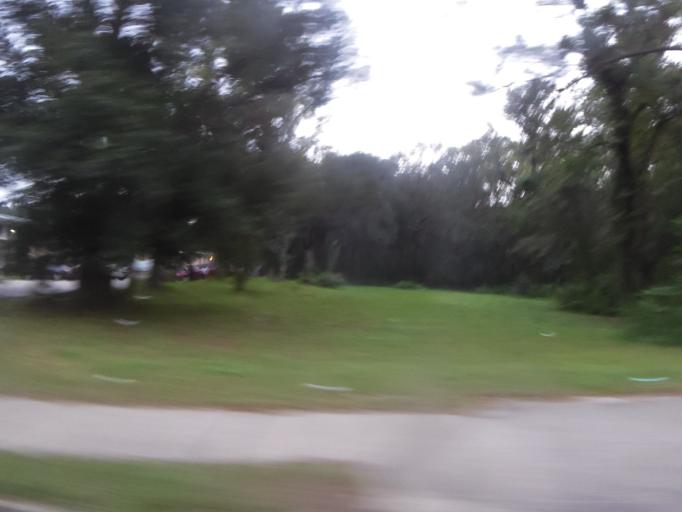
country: US
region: Florida
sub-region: Clay County
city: Bellair-Meadowbrook Terrace
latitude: 30.2723
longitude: -81.7476
